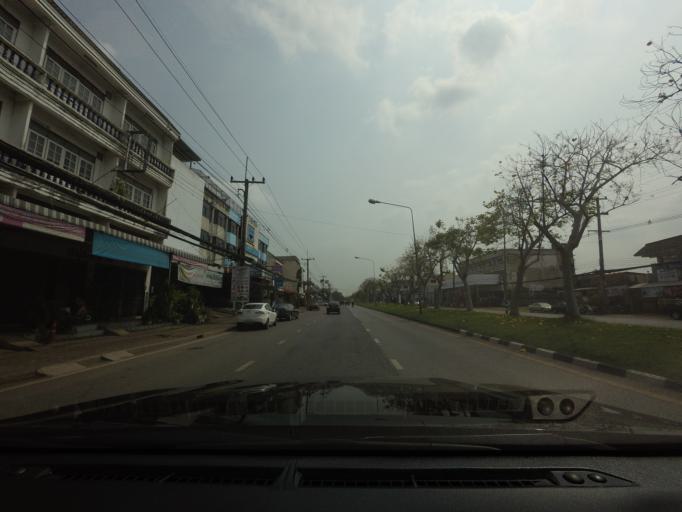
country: TH
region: Nakhon Nayok
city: Nakhon Nayok
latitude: 14.2106
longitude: 101.2052
